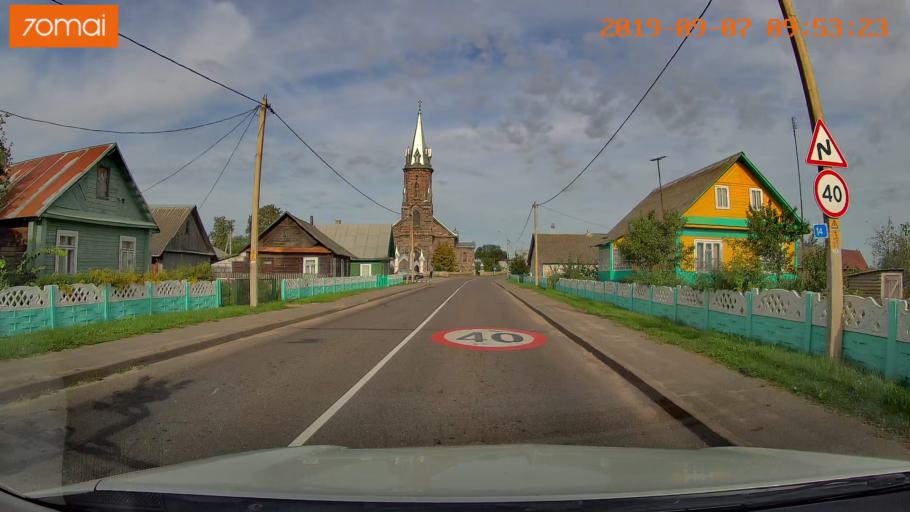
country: BY
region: Grodnenskaya
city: Iwye
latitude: 54.0069
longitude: 25.6057
